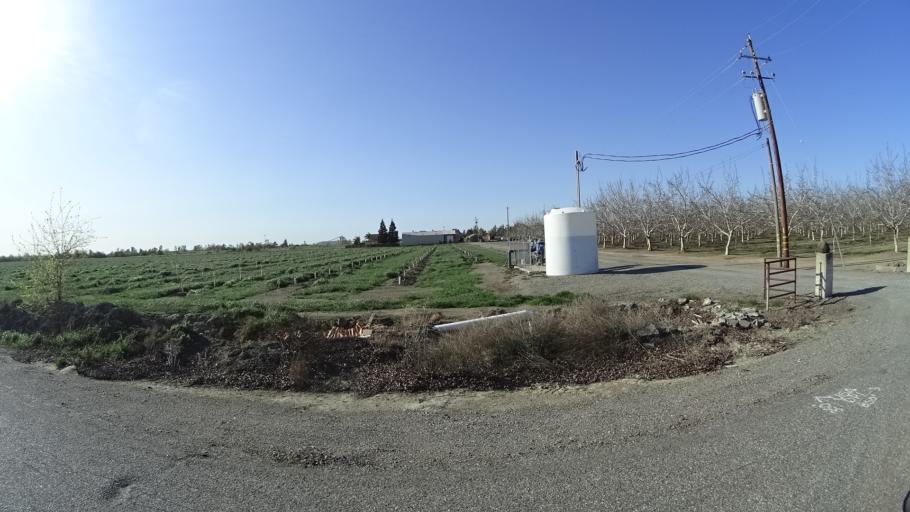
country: US
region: California
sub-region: Glenn County
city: Orland
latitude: 39.7573
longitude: -122.1186
